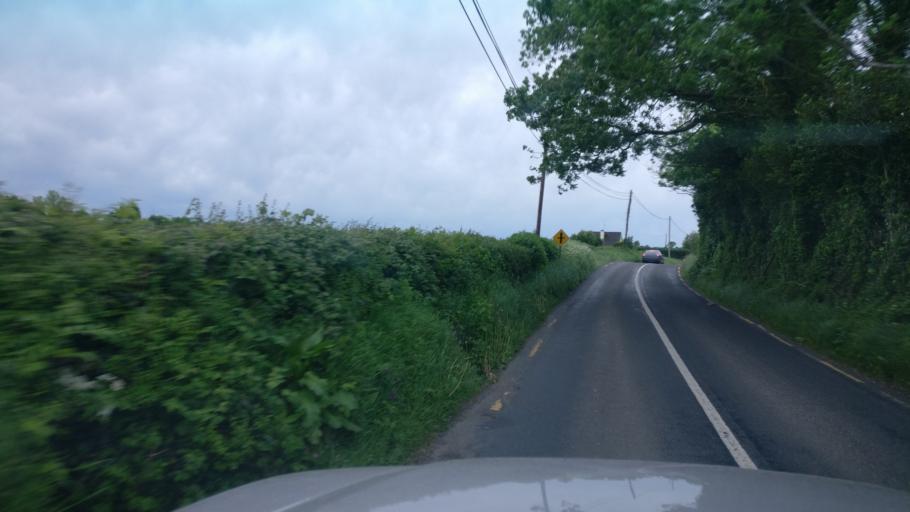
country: IE
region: Connaught
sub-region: County Galway
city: Portumna
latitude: 53.1227
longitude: -8.3288
